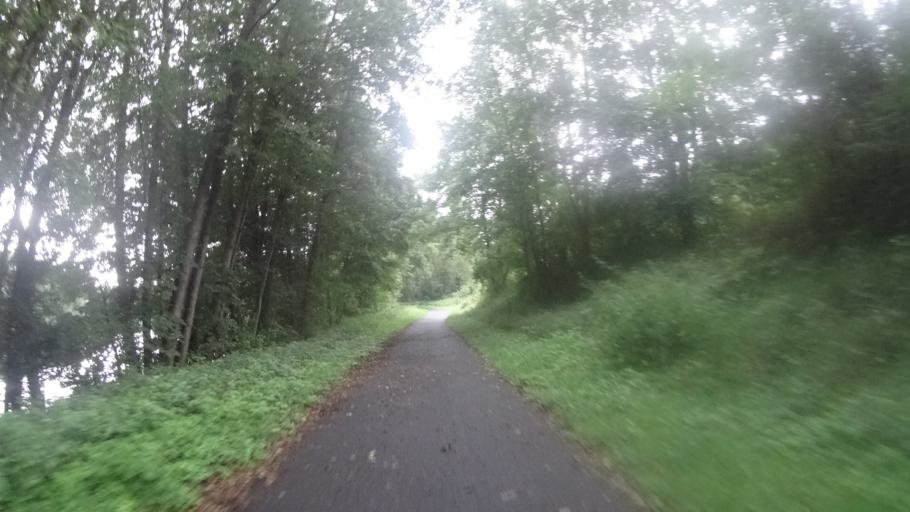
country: FR
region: Lorraine
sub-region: Departement de Meurthe-et-Moselle
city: Chaligny
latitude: 48.6379
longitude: 6.0399
